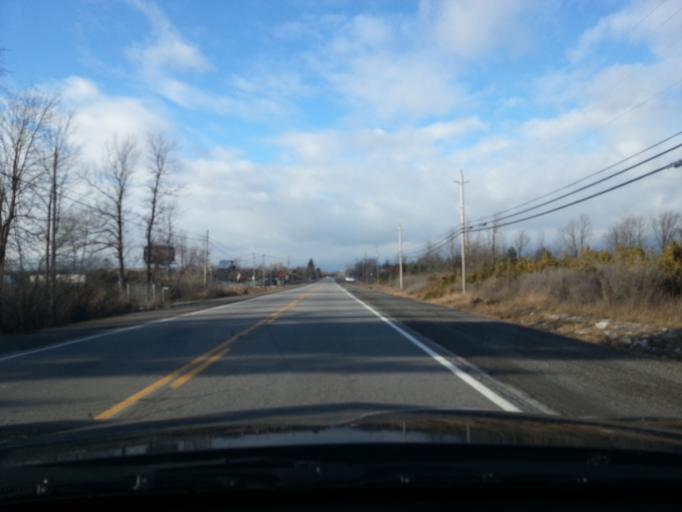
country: CA
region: Ontario
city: Ottawa
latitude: 45.2426
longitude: -75.5208
